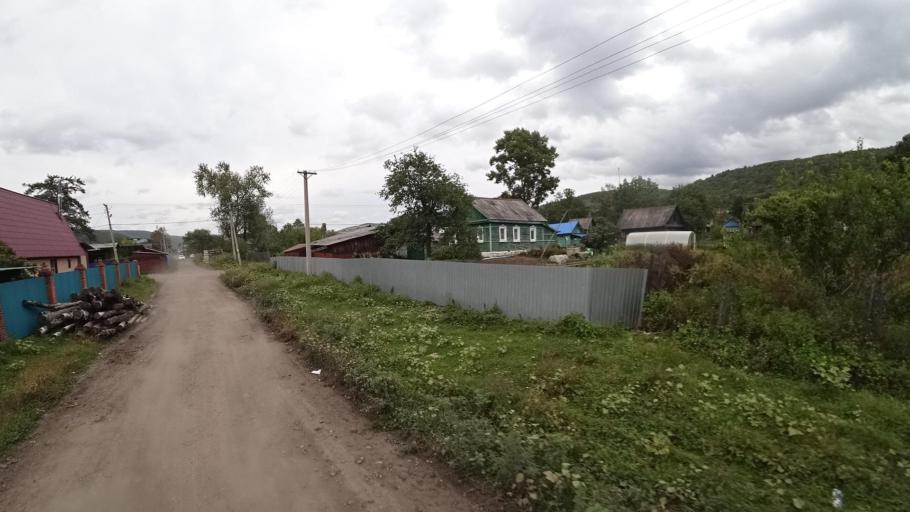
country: RU
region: Jewish Autonomous Oblast
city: Khingansk
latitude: 49.0044
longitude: 131.0521
